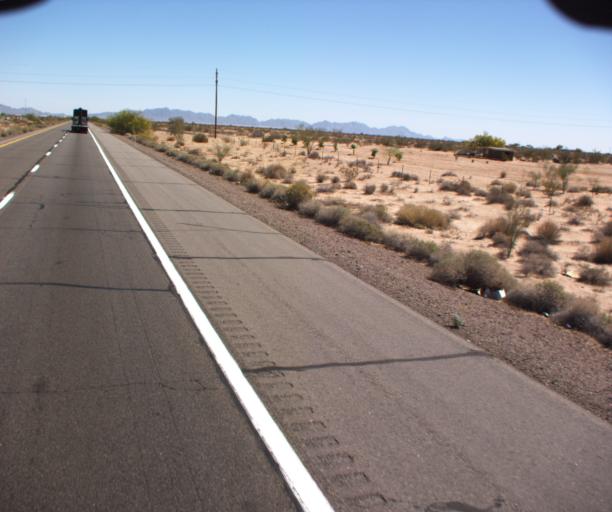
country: US
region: Arizona
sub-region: Yuma County
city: Wellton
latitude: 32.6879
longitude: -113.9892
